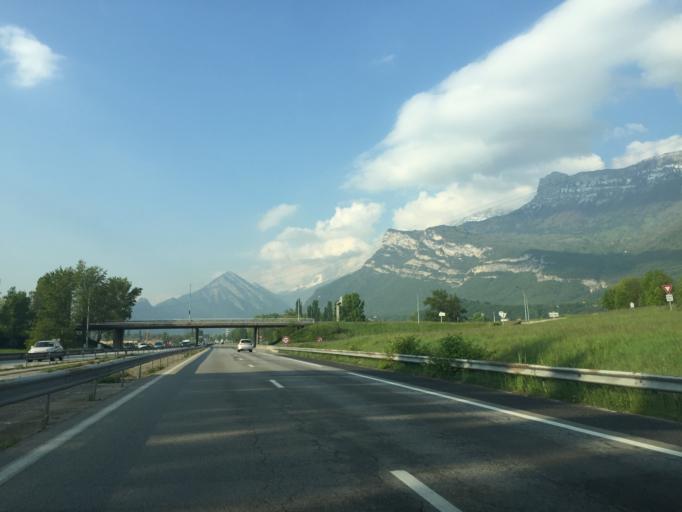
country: FR
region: Rhone-Alpes
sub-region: Departement de l'Isere
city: Claix
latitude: 45.1207
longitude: 5.6873
